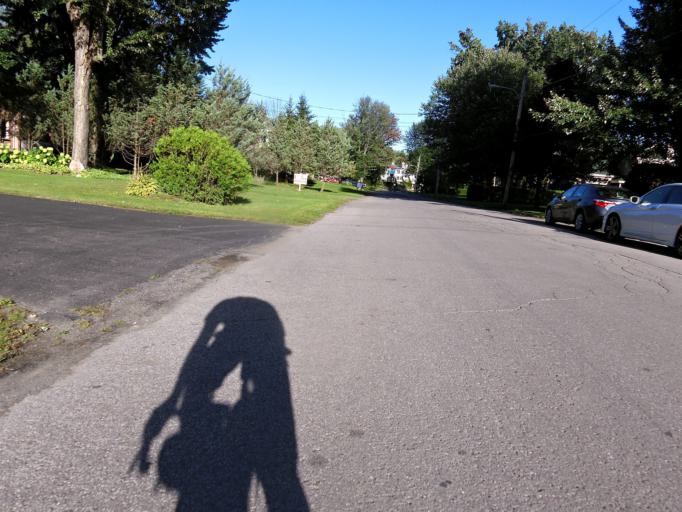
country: CA
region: Quebec
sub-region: Outaouais
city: Gatineau
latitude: 45.4765
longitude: -75.6204
